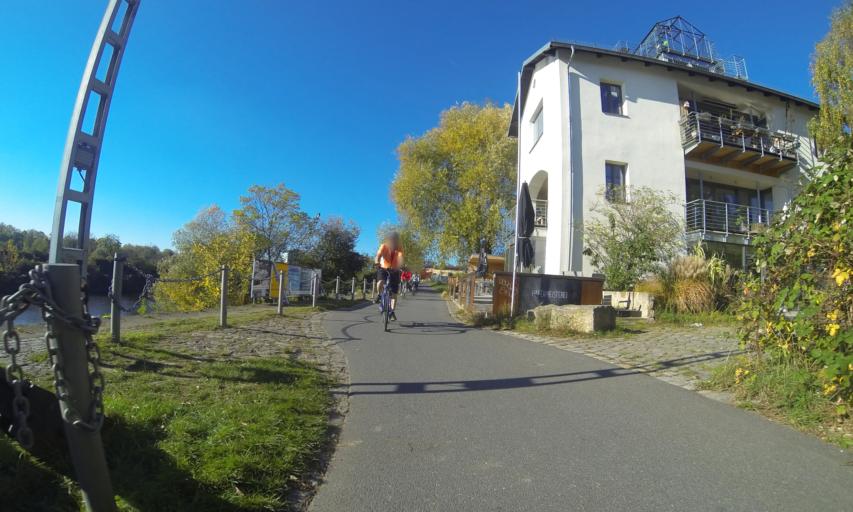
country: DE
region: Saxony
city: Dresden
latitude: 51.0669
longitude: 13.7307
